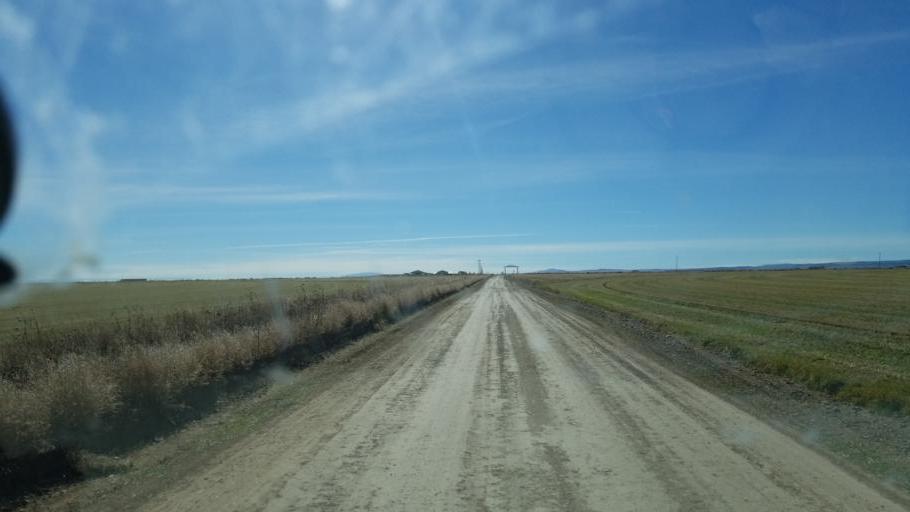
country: US
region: Colorado
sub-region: Rio Grande County
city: Monte Vista
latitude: 37.4051
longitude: -106.1305
